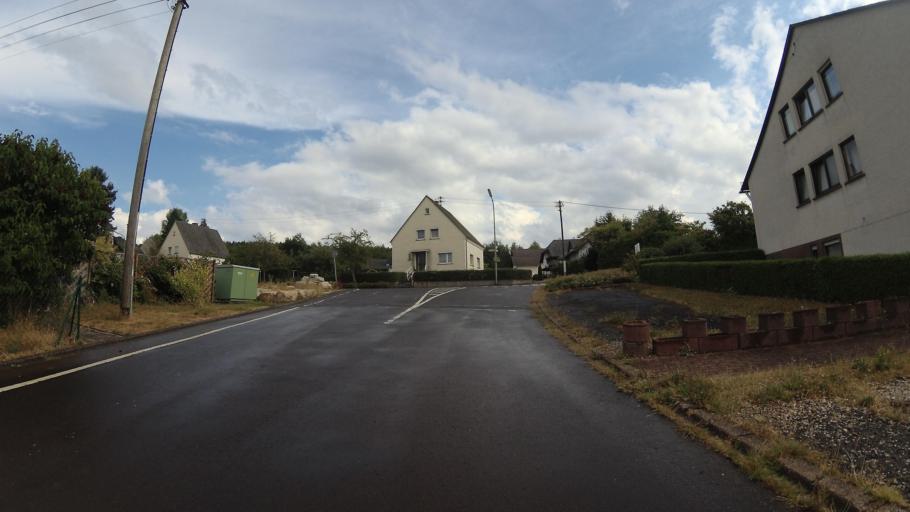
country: DE
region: Rheinland-Pfalz
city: Rorodt
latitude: 49.7732
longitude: 7.0957
